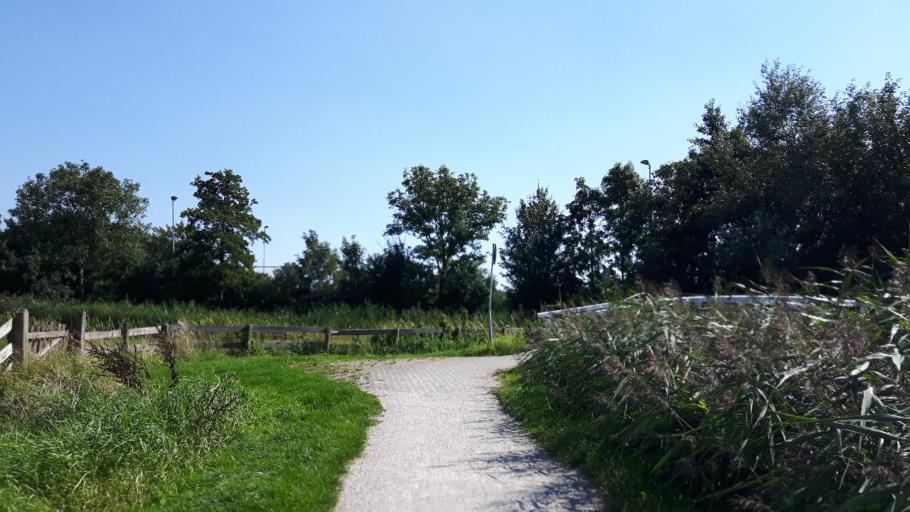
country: NL
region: Friesland
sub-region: Sudwest Fryslan
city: IJlst
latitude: 53.0130
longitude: 5.6275
